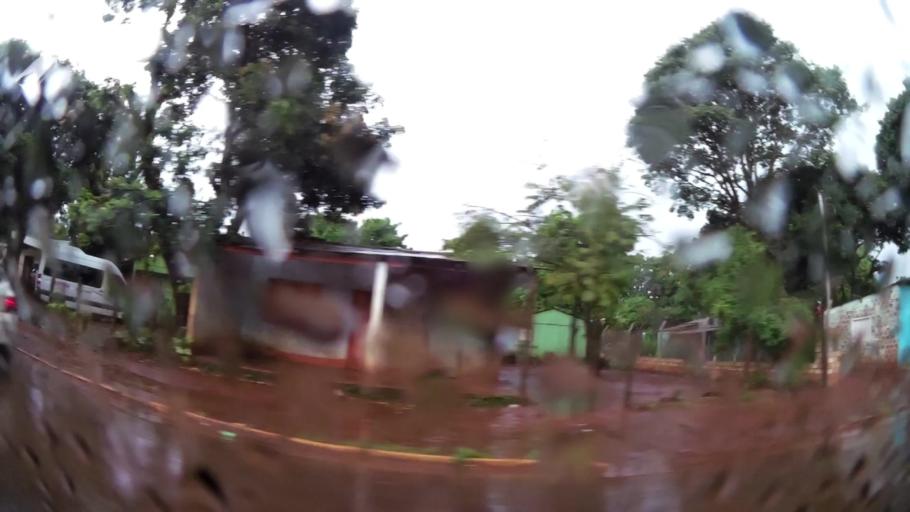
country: PY
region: Alto Parana
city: Presidente Franco
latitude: -25.5462
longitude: -54.6758
